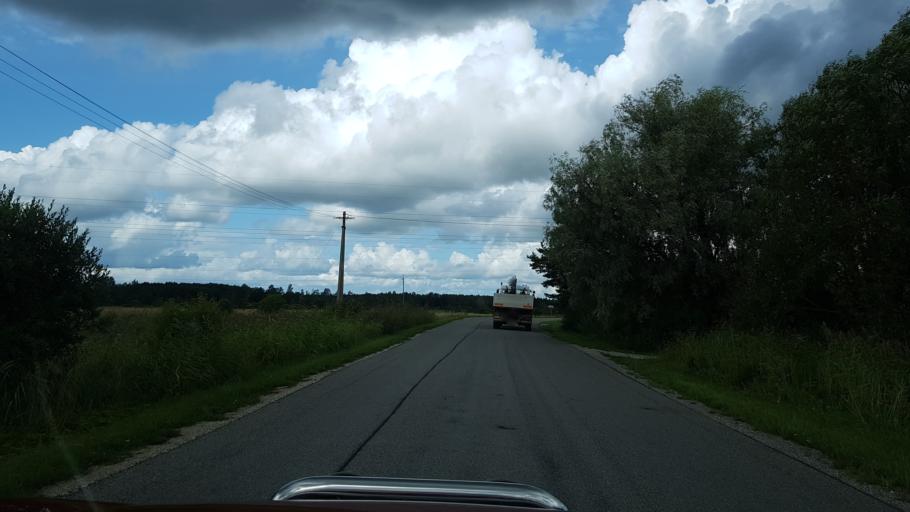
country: EE
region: Laeaene
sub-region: Lihula vald
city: Lihula
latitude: 58.6940
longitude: 23.8326
